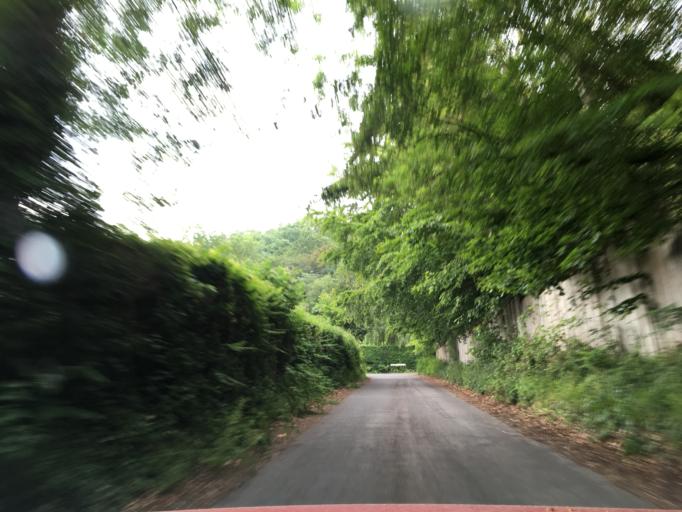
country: GB
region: England
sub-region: North Somerset
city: Clevedon
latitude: 51.4482
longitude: -2.8164
